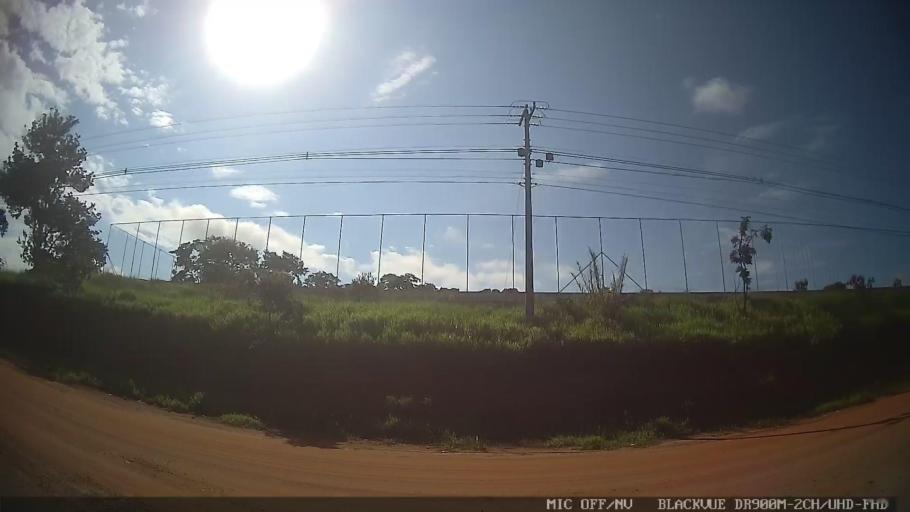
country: BR
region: Sao Paulo
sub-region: Jarinu
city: Jarinu
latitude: -23.0688
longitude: -46.6857
